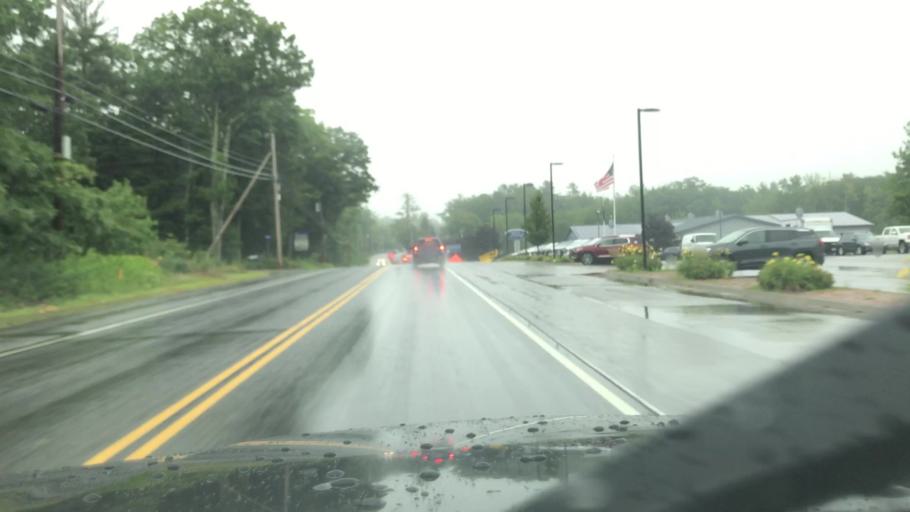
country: US
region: Maine
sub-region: York County
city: Kennebunk
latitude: 43.4192
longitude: -70.5171
